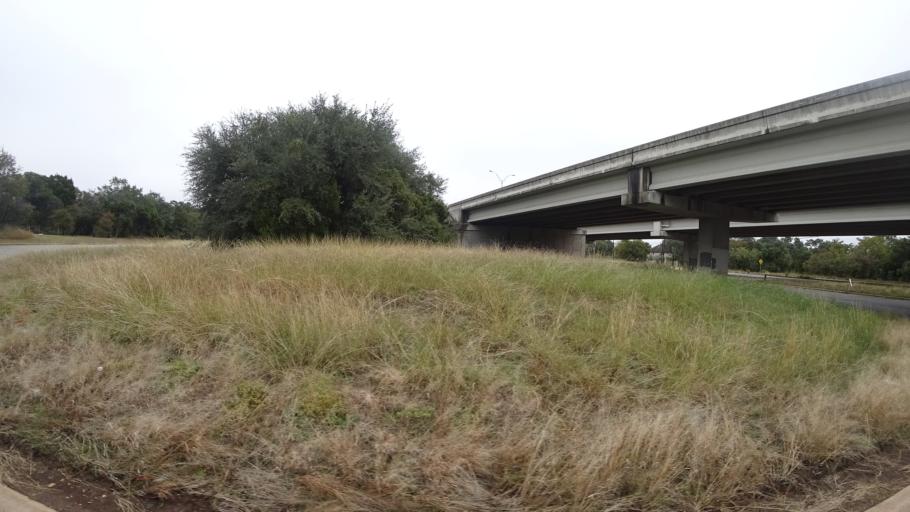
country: US
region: Texas
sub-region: Travis County
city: Shady Hollow
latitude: 30.2169
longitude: -97.8449
